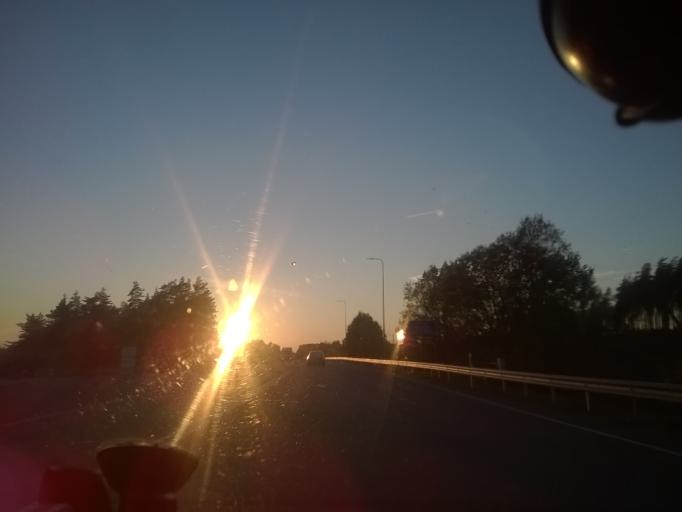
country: EE
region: Laeaene
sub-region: Lihula vald
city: Lihula
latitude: 58.9731
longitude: 23.9023
